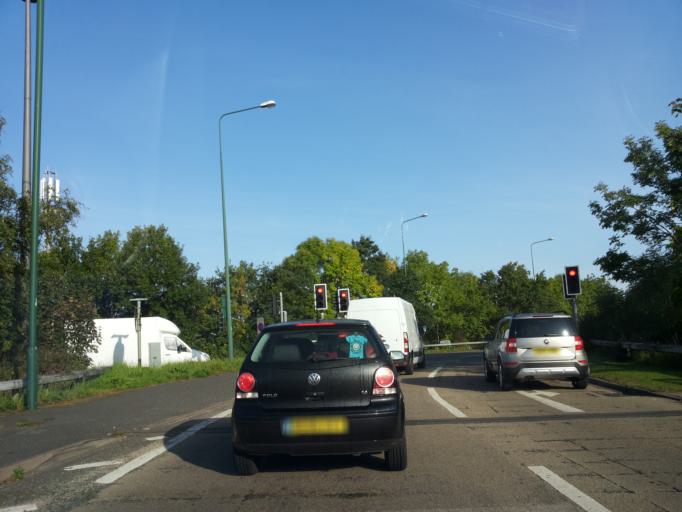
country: GB
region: England
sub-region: Solihull
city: Knowle
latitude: 52.4048
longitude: -1.7507
